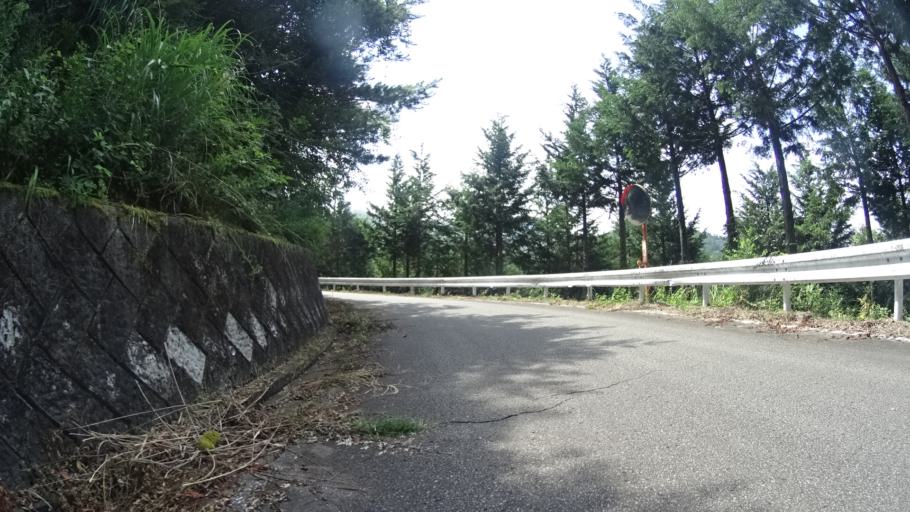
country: JP
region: Yamanashi
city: Nirasaki
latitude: 35.8847
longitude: 138.4781
